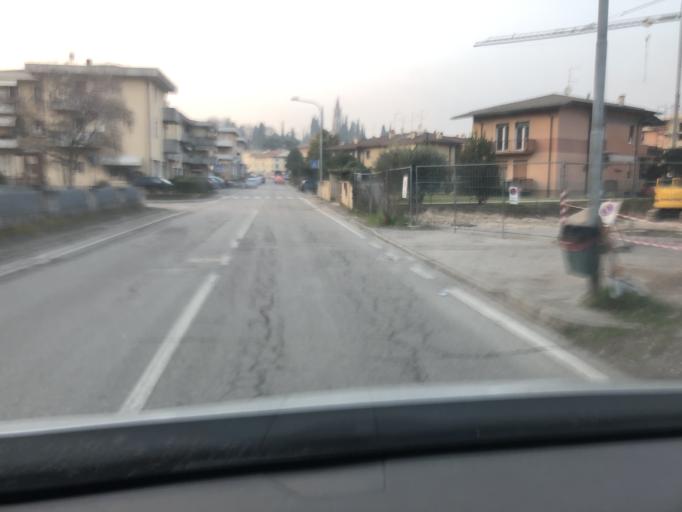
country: IT
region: Veneto
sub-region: Provincia di Verona
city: Sommacampagna
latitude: 45.4039
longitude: 10.8479
